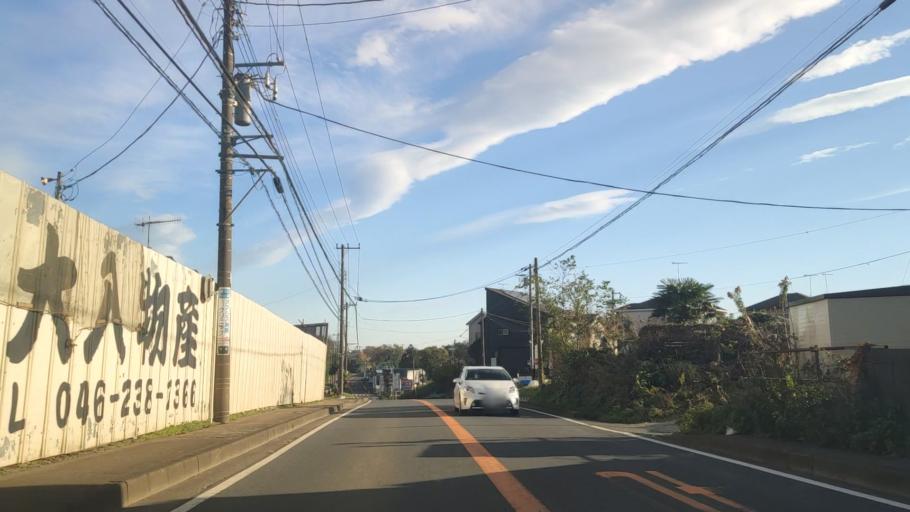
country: JP
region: Kanagawa
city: Atsugi
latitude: 35.4144
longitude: 139.4031
